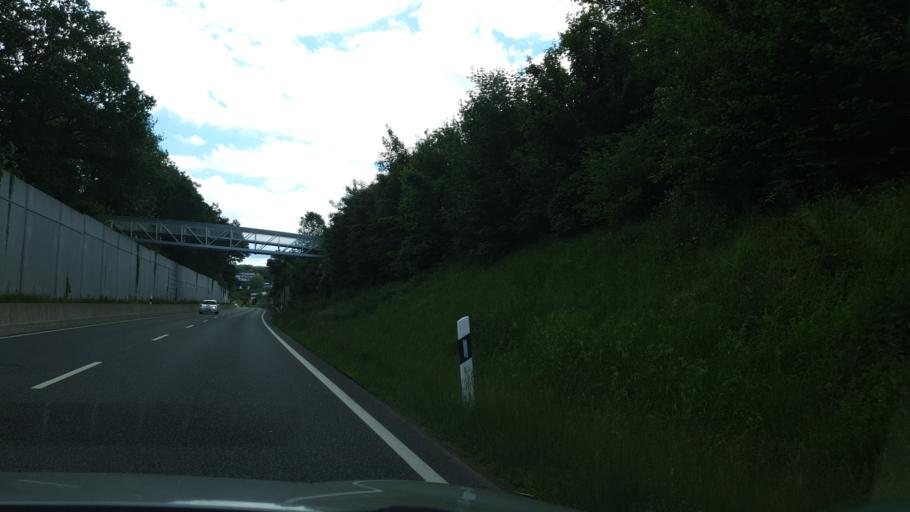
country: DE
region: Rheinland-Pfalz
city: Hohr-Grenzhausen
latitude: 50.4356
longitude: 7.6769
